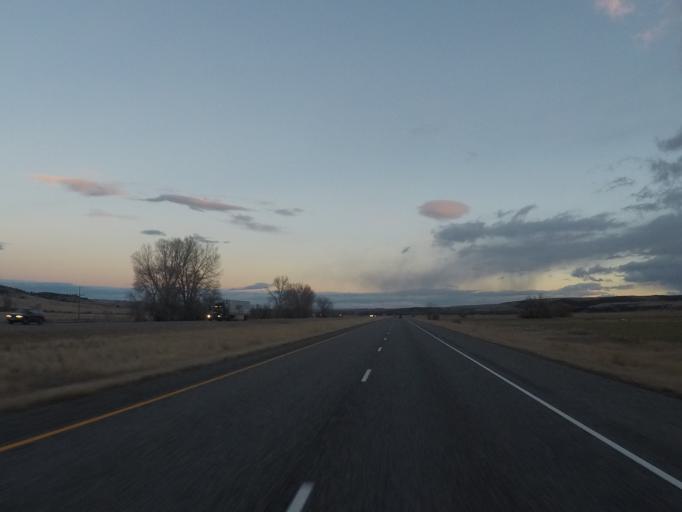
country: US
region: Montana
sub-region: Sweet Grass County
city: Big Timber
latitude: 45.8091
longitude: -109.8604
